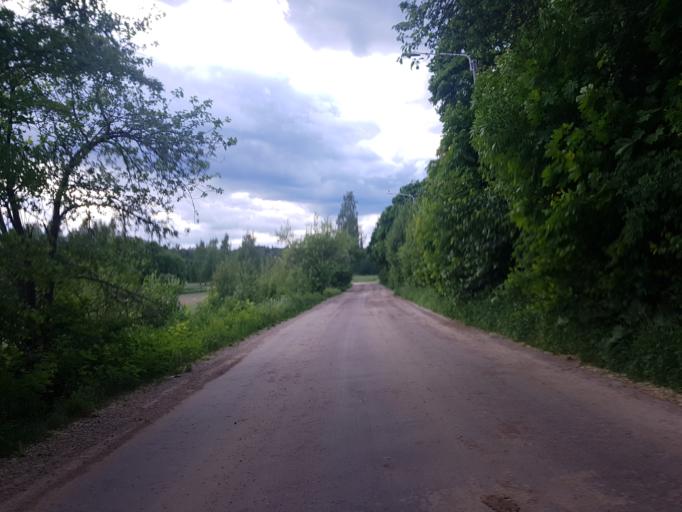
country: FI
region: Uusimaa
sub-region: Helsinki
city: Vantaa
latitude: 60.2555
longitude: 24.9658
